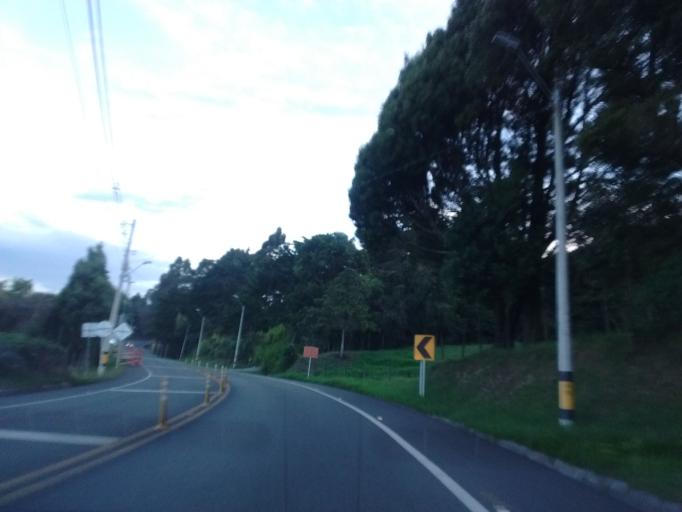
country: CO
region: Antioquia
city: Envigado
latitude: 6.1700
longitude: -75.5012
